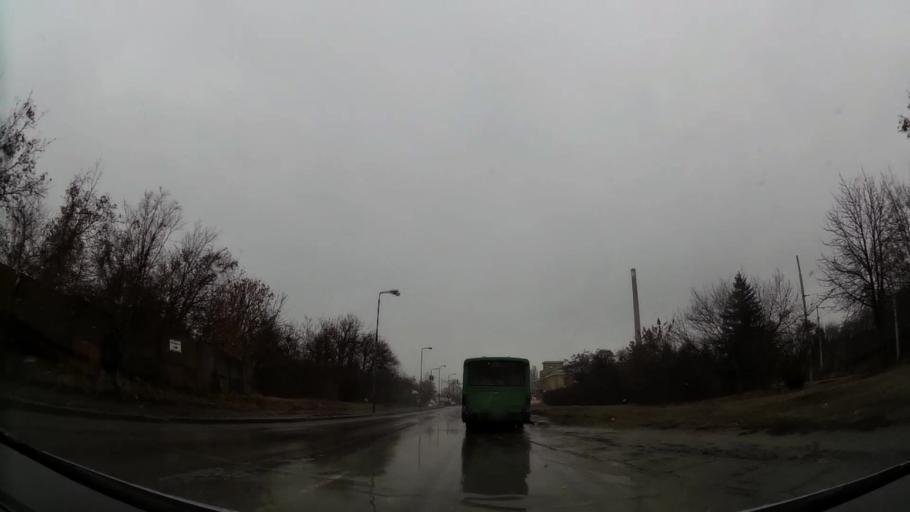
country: BG
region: Sofia-Capital
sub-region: Stolichna Obshtina
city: Sofia
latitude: 42.6632
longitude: 23.4143
